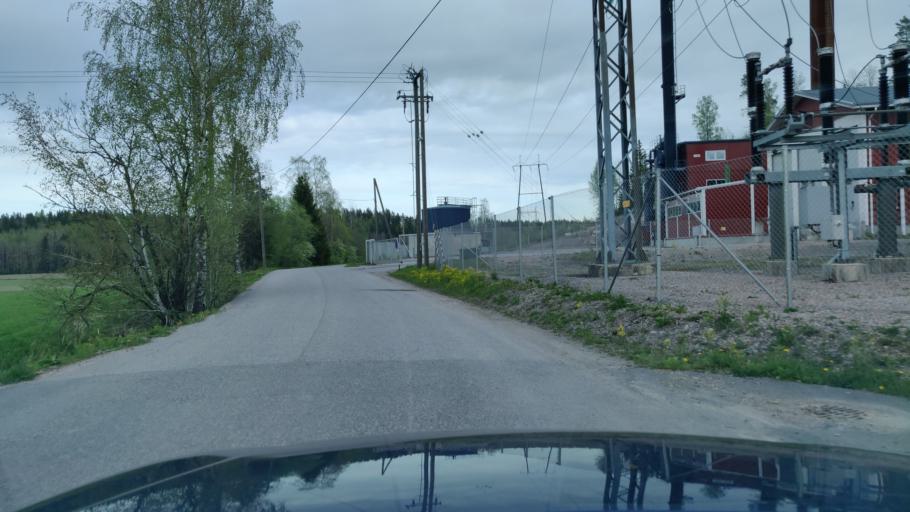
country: FI
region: Uusimaa
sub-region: Helsinki
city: Nurmijaervi
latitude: 60.3845
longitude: 24.7643
